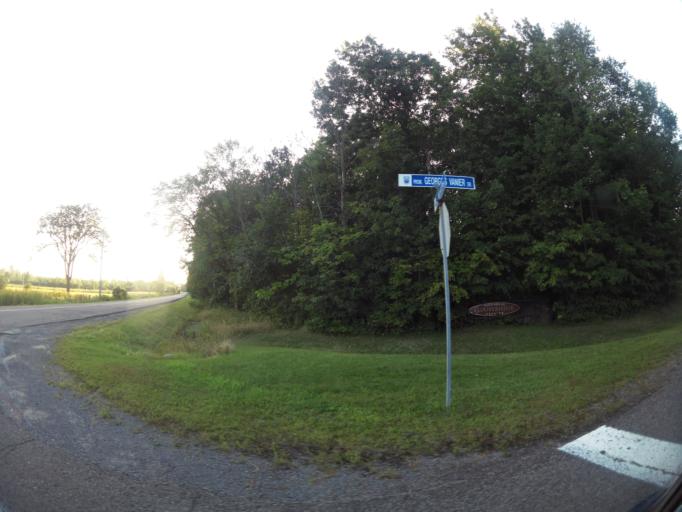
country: CA
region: Ontario
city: Clarence-Rockland
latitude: 45.4996
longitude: -75.4306
